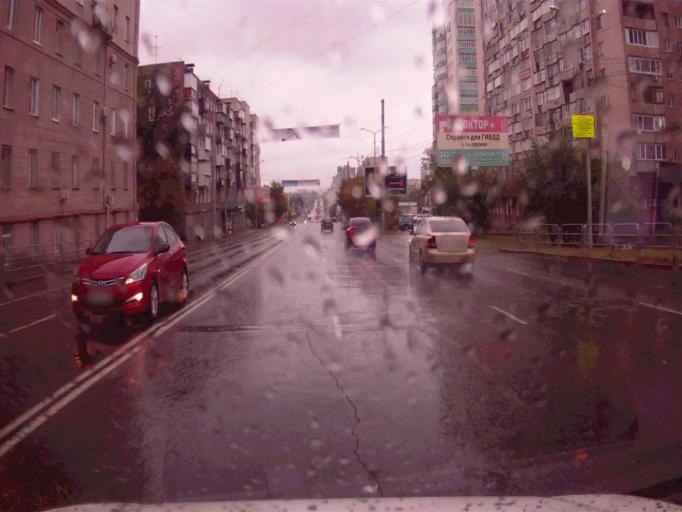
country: RU
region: Chelyabinsk
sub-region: Gorod Chelyabinsk
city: Chelyabinsk
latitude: 55.1611
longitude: 61.4164
